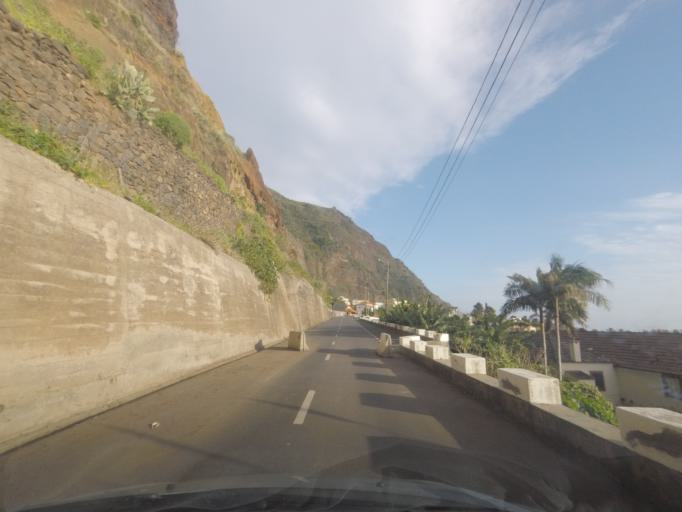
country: PT
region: Madeira
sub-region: Calheta
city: Arco da Calheta
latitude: 32.7033
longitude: -17.1373
